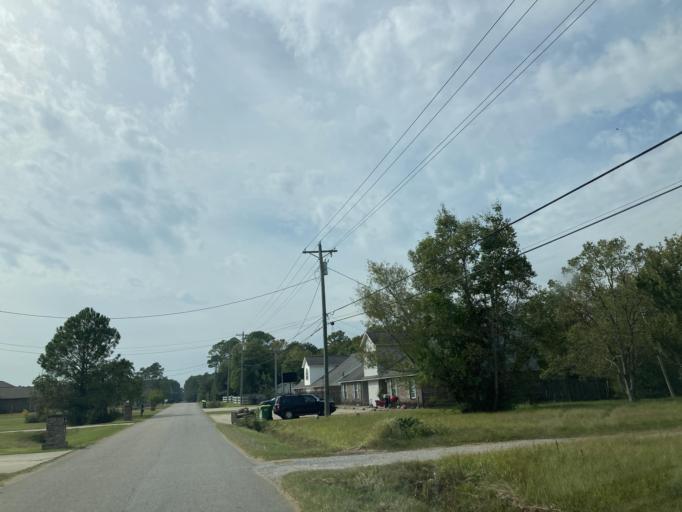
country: US
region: Mississippi
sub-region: Jackson County
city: Gulf Hills
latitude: 30.4704
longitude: -88.8433
